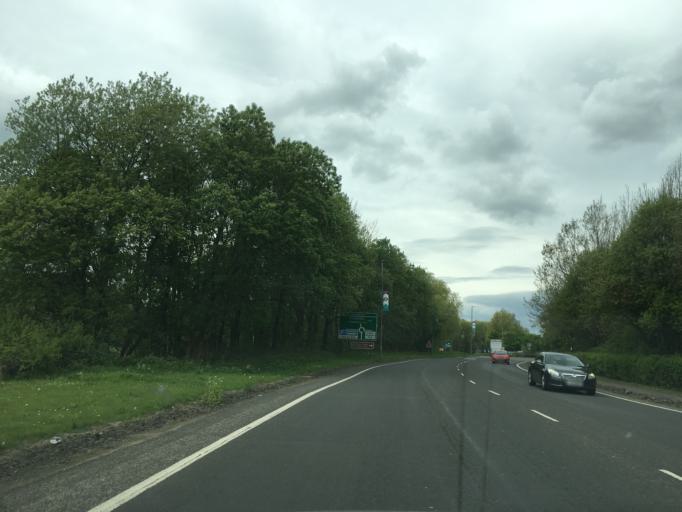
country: GB
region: Scotland
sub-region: Stirling
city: Stirling
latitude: 56.1284
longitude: -3.9630
